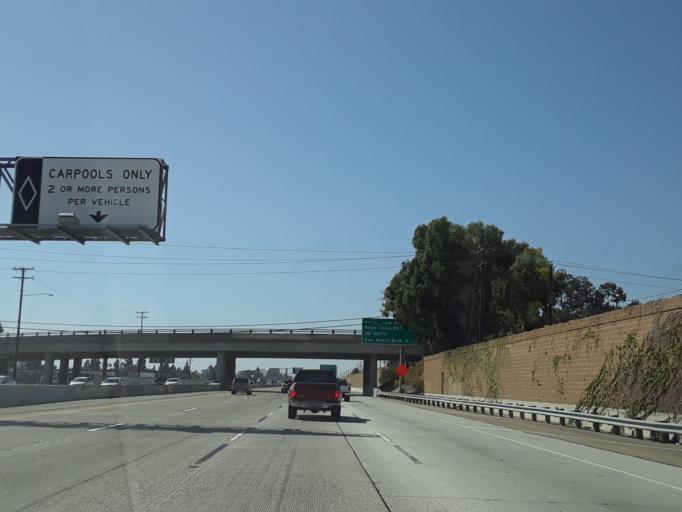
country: US
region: California
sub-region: Orange County
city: Westminster
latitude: 33.7744
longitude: -118.0190
